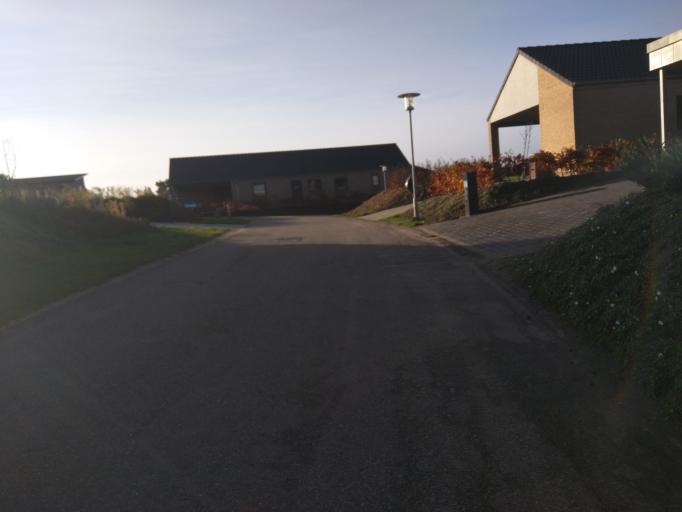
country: DK
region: Central Jutland
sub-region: Viborg Kommune
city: Viborg
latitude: 56.4396
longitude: 9.3722
